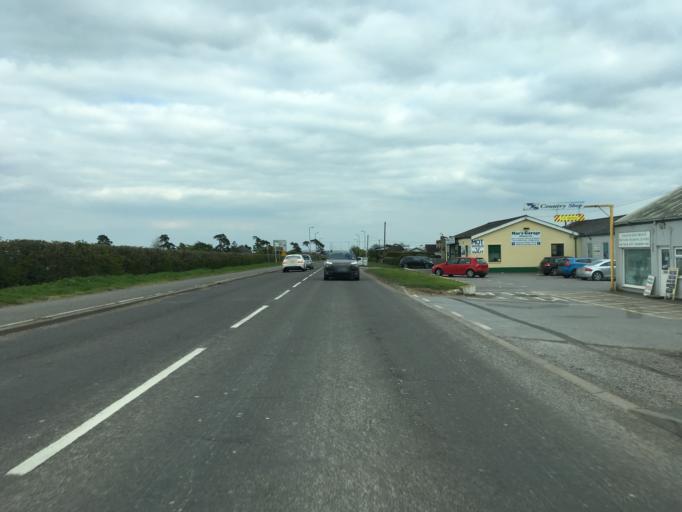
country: GB
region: England
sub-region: Oxfordshire
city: Witney
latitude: 51.7940
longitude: -1.5250
